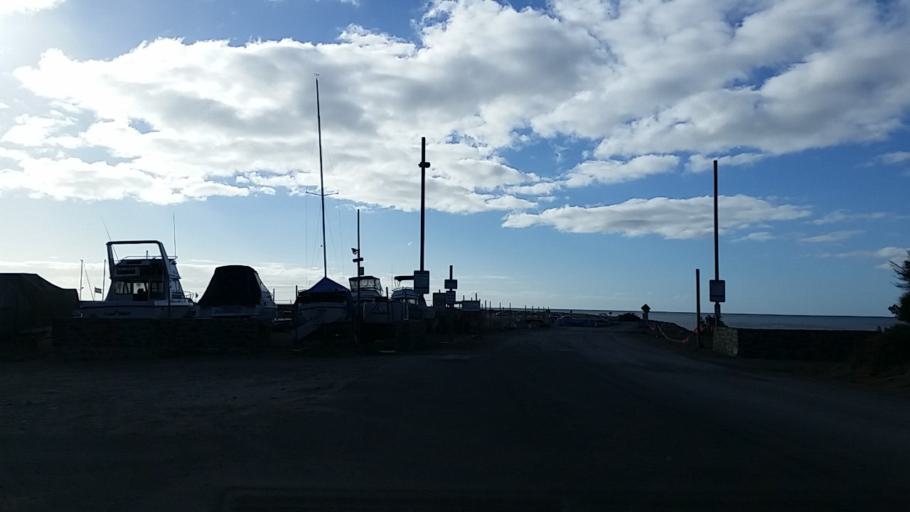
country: AU
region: South Australia
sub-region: Yankalilla
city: Normanville
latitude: -35.5013
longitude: 138.2448
